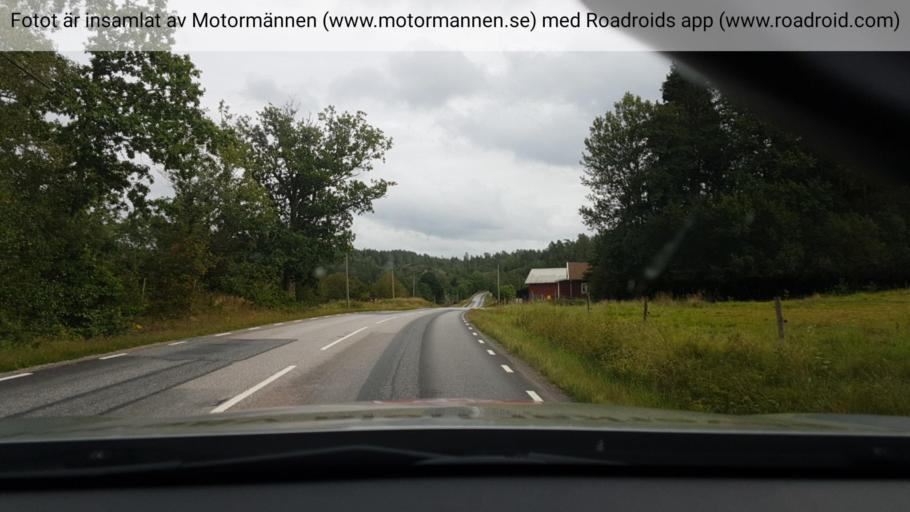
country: SE
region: Vaestra Goetaland
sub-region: Sotenas Kommun
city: Hunnebostrand
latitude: 58.5623
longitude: 11.3943
